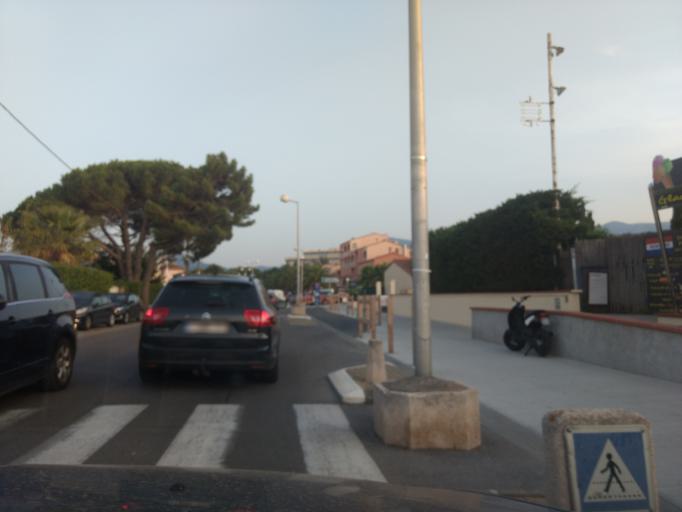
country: FR
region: Languedoc-Roussillon
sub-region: Departement des Pyrenees-Orientales
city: Argelers
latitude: 42.5555
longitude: 3.0426
